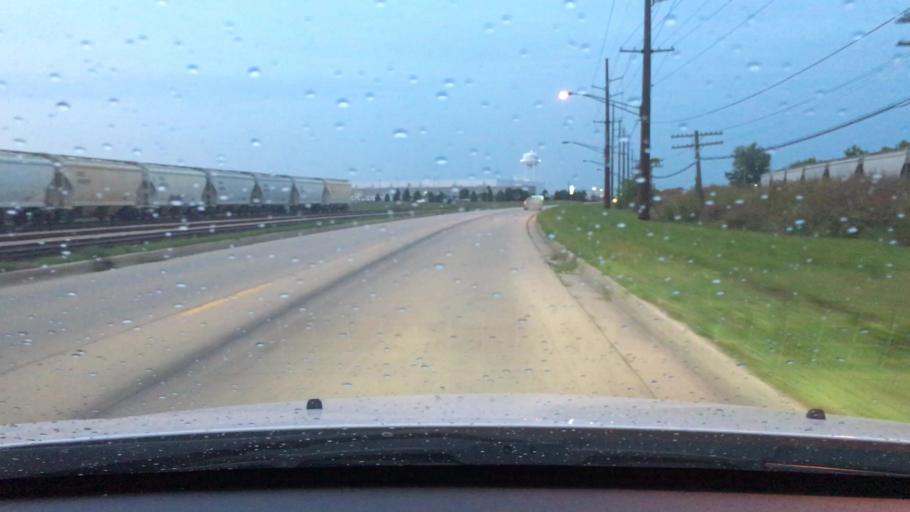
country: US
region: Illinois
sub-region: Ogle County
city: Rochelle
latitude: 41.9161
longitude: -89.0508
